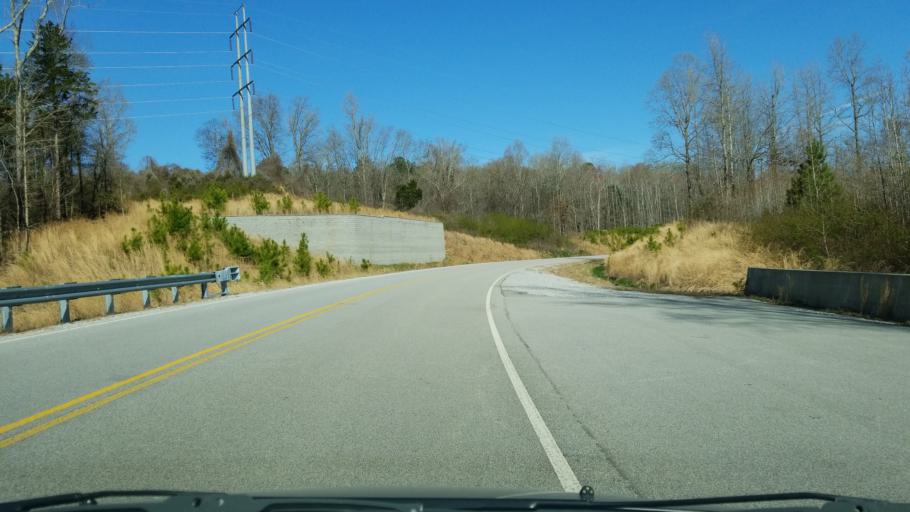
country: US
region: Tennessee
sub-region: Hamilton County
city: Harrison
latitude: 35.0955
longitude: -85.1359
